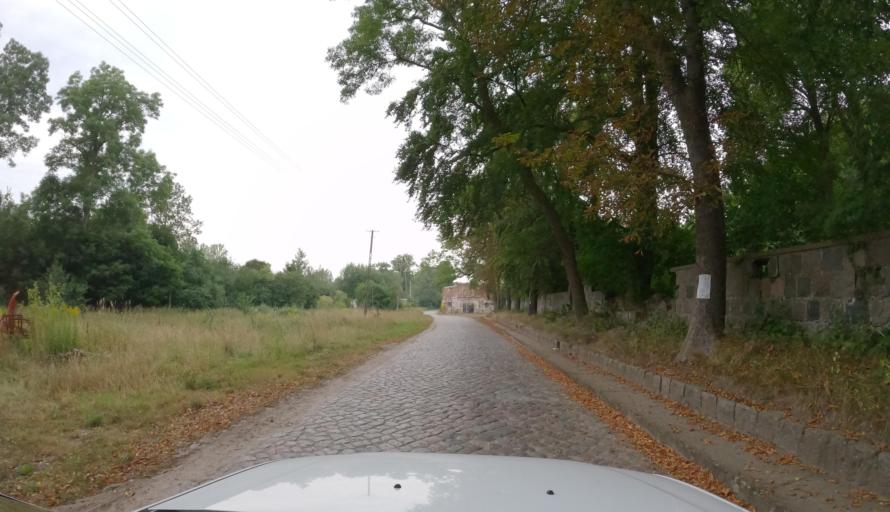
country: PL
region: West Pomeranian Voivodeship
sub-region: Powiat kolobrzeski
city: Ryman
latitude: 53.8464
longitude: 15.5922
